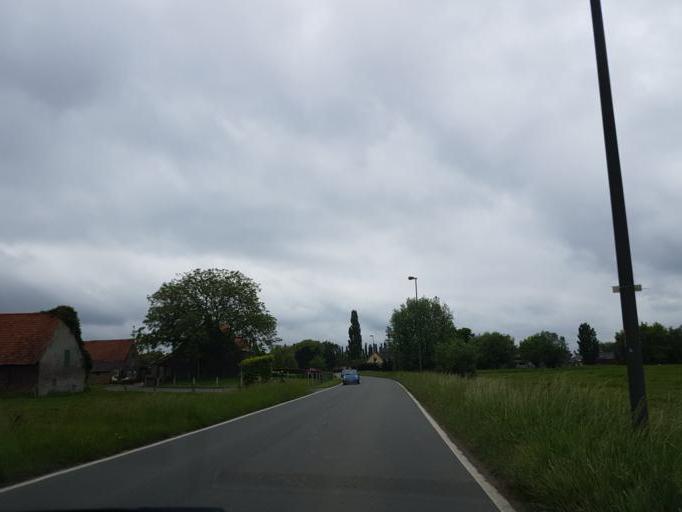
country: BE
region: Flanders
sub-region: Provincie Oost-Vlaanderen
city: Zomergem
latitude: 51.1056
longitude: 3.5663
